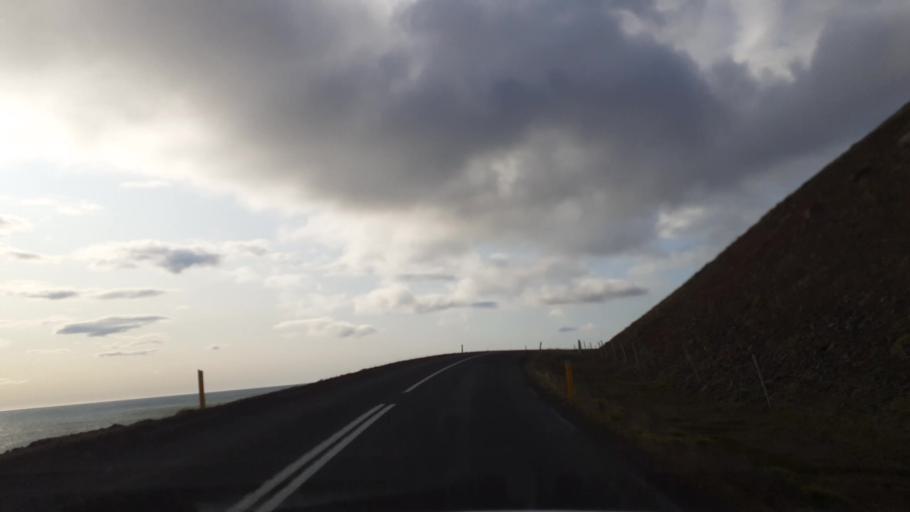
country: IS
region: East
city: Eskifjoerdur
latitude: 64.7379
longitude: -13.9913
